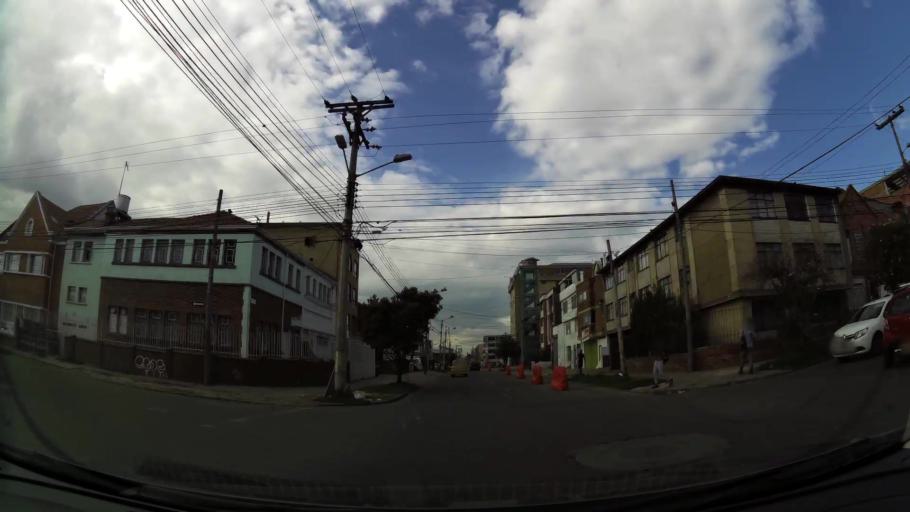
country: CO
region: Bogota D.C.
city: Bogota
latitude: 4.6484
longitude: -74.0670
